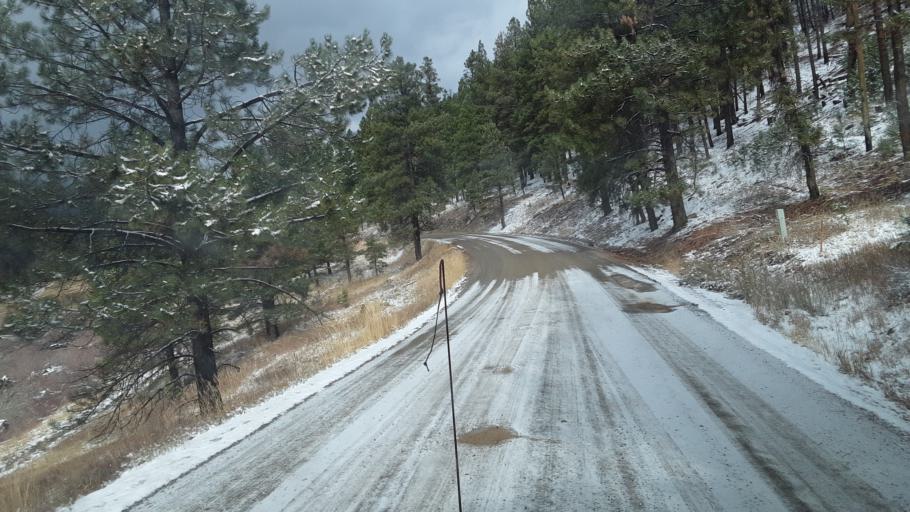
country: US
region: Colorado
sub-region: La Plata County
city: Bayfield
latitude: 37.4253
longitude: -107.5379
